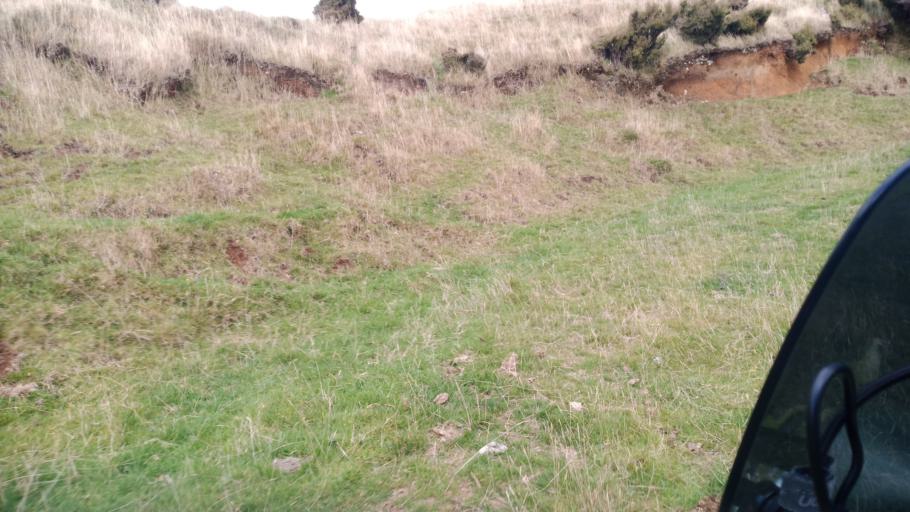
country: NZ
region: Gisborne
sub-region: Gisborne District
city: Gisborne
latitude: -38.4696
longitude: 177.5342
